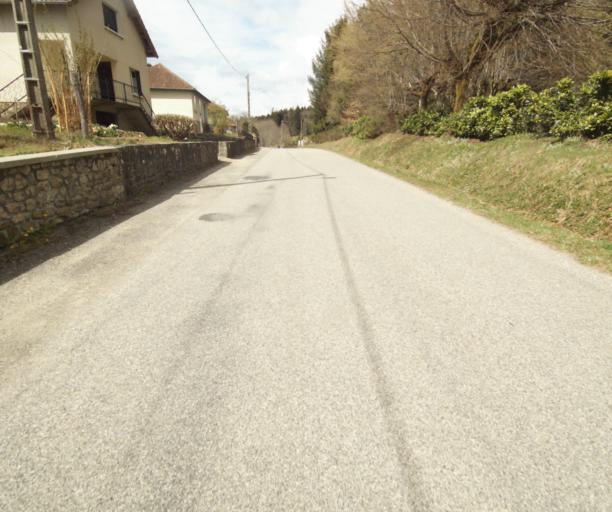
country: FR
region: Limousin
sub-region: Departement de la Correze
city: Correze
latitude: 45.2698
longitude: 1.9775
